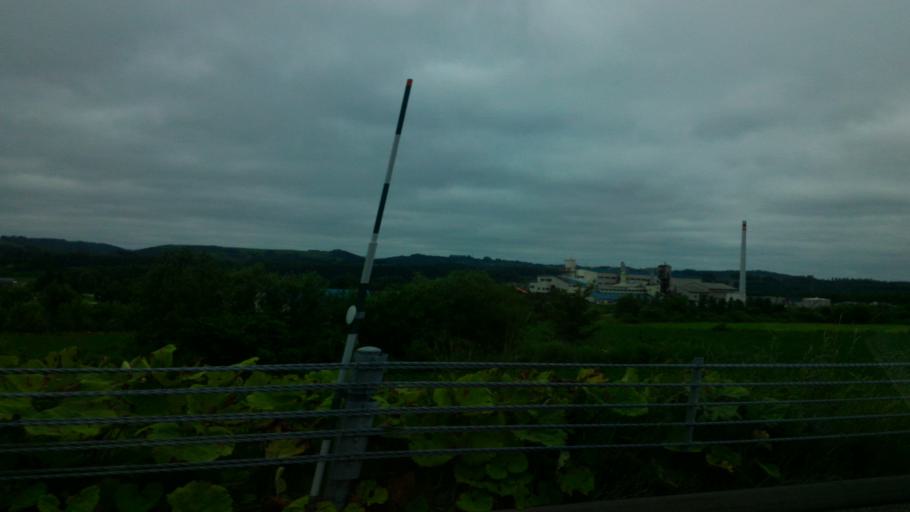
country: JP
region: Hokkaido
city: Otofuke
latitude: 43.0994
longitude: 143.5440
